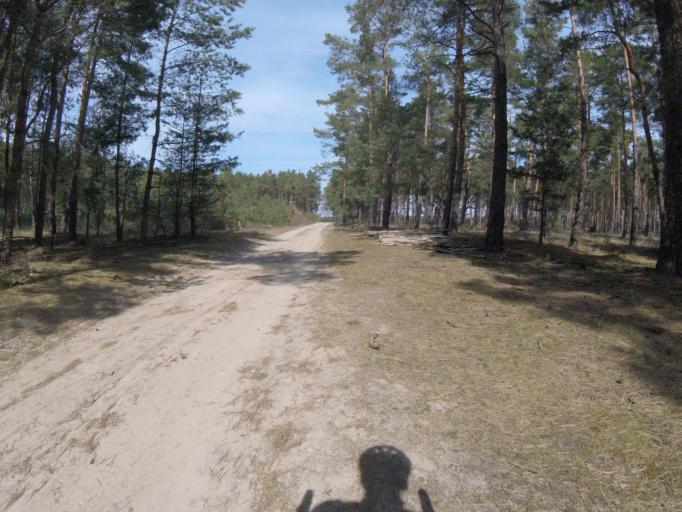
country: DE
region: Brandenburg
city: Bestensee
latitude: 52.2148
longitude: 13.6629
